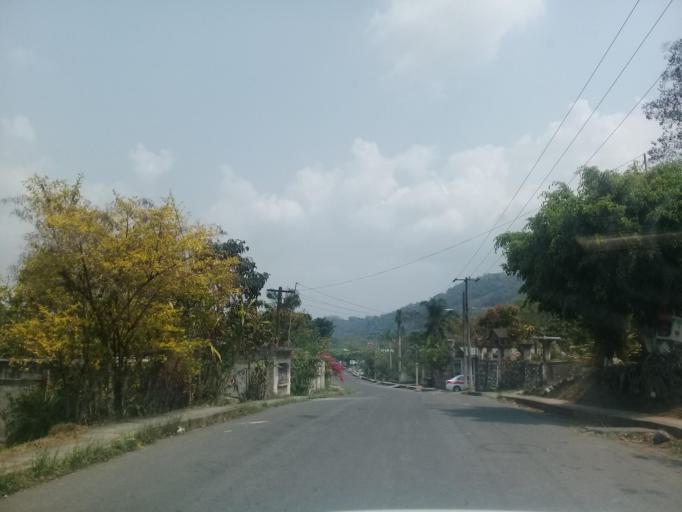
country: MX
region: Veracruz
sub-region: Cordoba
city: San Jose de Tapia
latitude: 18.8152
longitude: -96.9829
